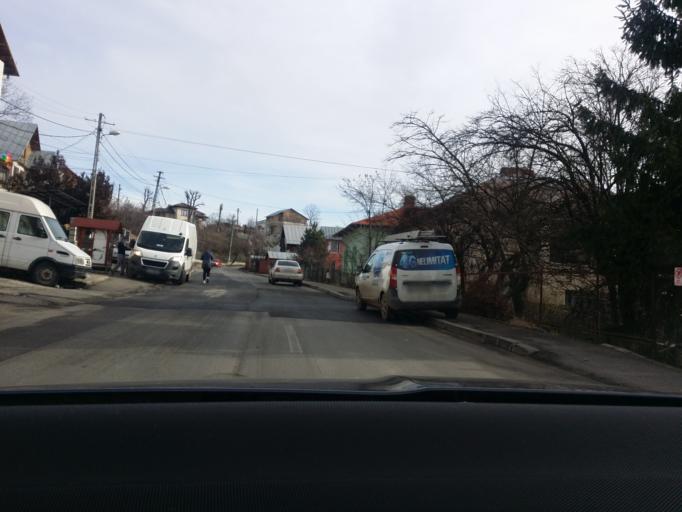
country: RO
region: Prahova
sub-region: Municipiul Campina
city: Campina
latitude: 45.1267
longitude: 25.7247
